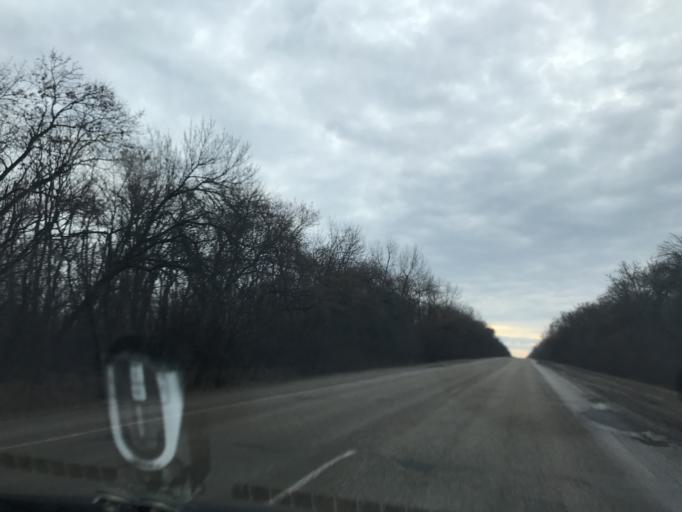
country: RU
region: Krasnodarskiy
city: Mirskoy
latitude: 45.5658
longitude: 40.4268
